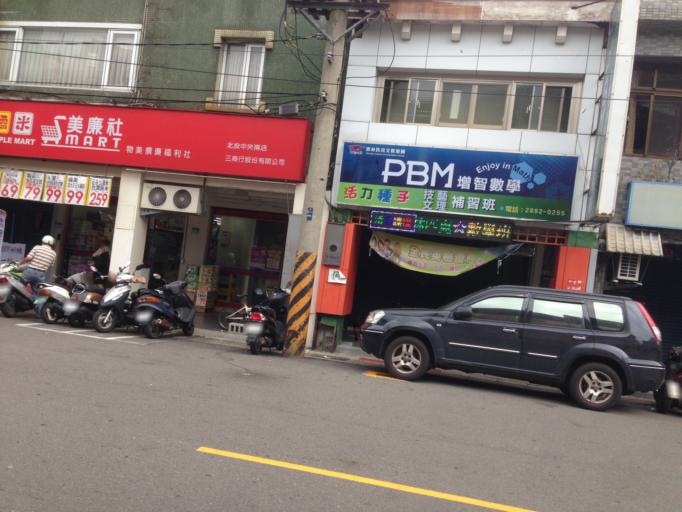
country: TW
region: Taipei
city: Taipei
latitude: 25.1300
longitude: 121.5013
